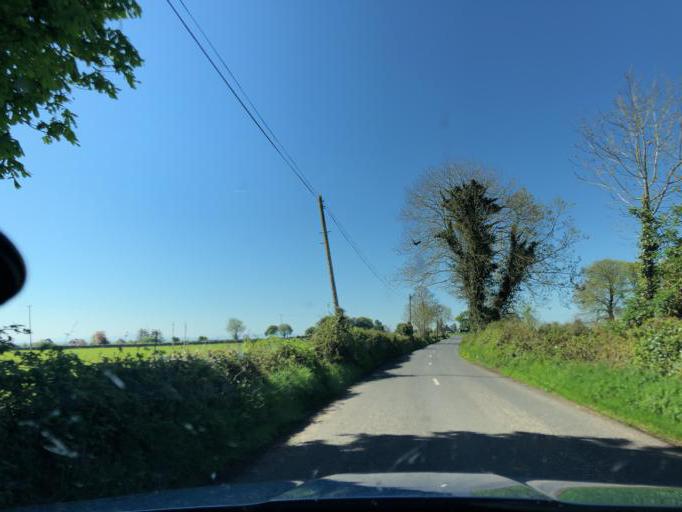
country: IE
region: Connaught
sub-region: County Galway
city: Portumna
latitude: 53.1728
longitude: -8.2079
